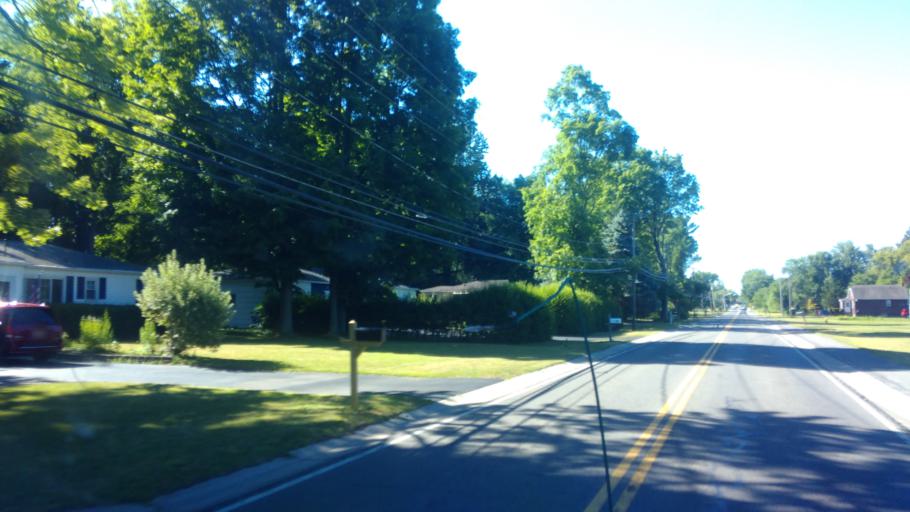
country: US
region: New York
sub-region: Monroe County
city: Webster
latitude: 43.2224
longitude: -77.4613
